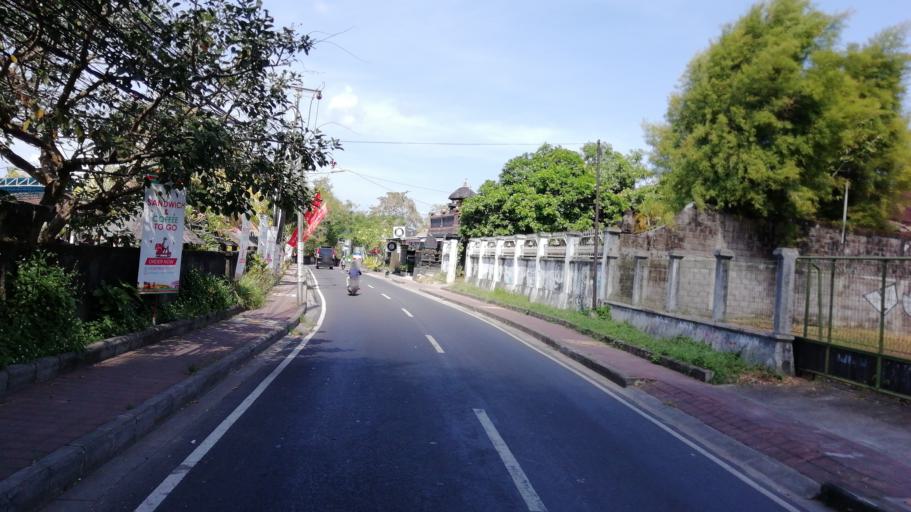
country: ID
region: Bali
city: Banjar Gunungpande
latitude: -8.6411
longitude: 115.1429
